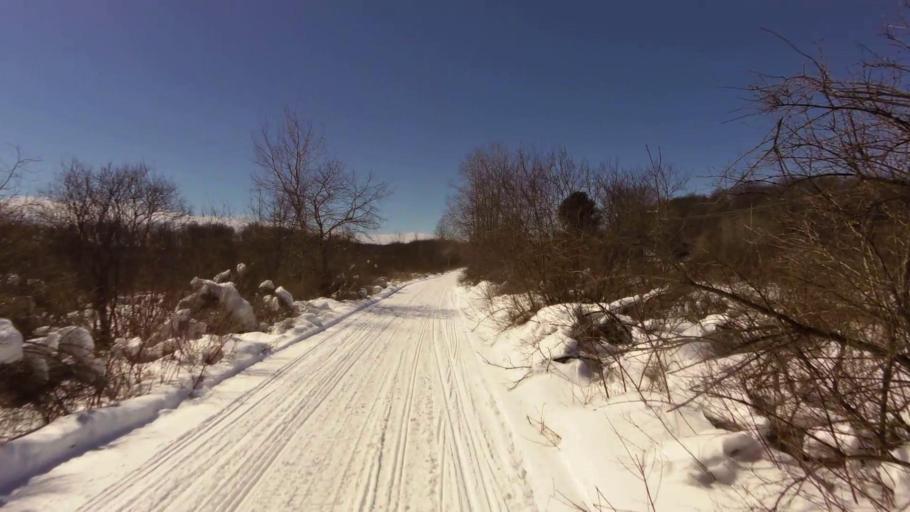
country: US
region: New York
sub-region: Wyoming County
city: Arcade
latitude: 42.4244
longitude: -78.3659
